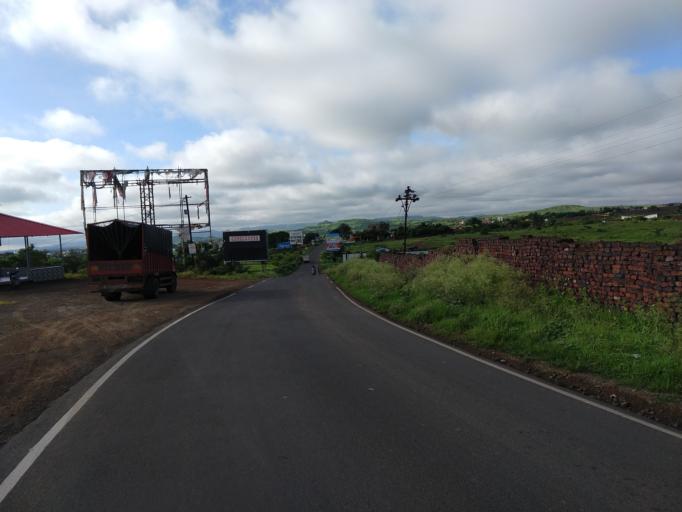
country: IN
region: Maharashtra
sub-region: Pune Division
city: Khed
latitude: 18.3990
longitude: 73.9135
